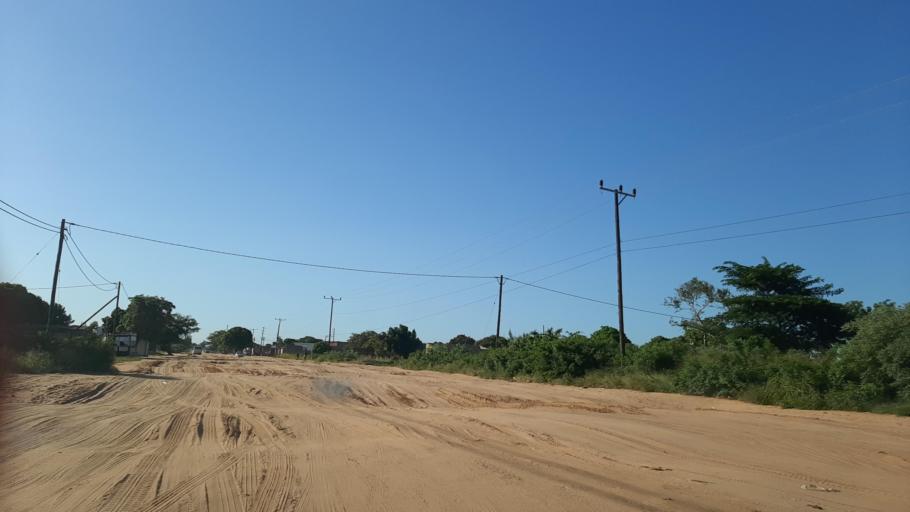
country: MZ
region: Maputo City
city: Maputo
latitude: -25.7490
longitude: 32.5460
